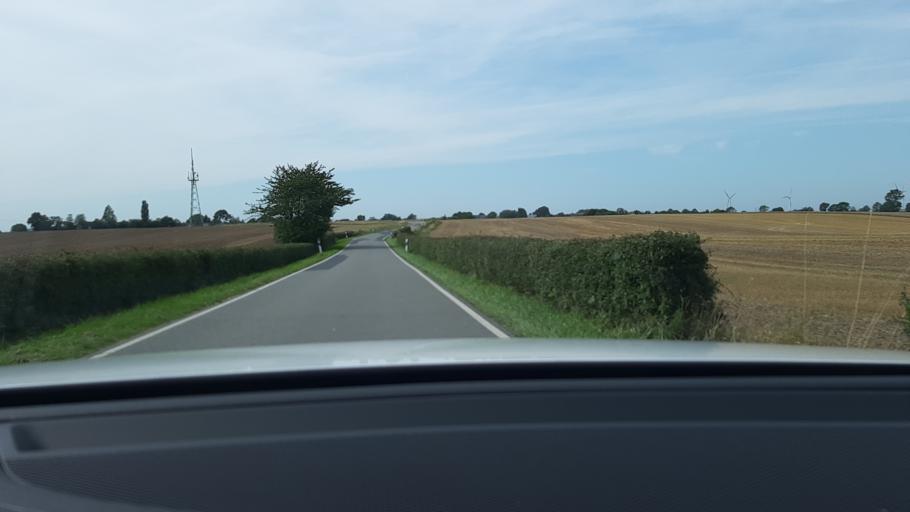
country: DE
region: Schleswig-Holstein
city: Rehhorst
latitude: 53.8716
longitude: 10.4820
